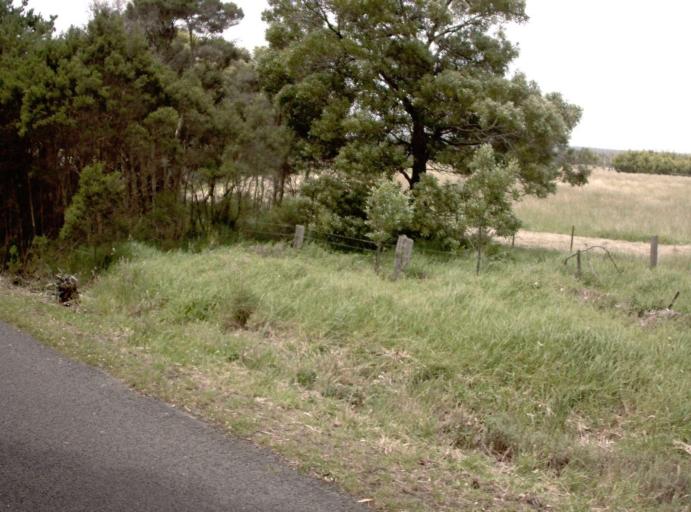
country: AU
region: Victoria
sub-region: Latrobe
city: Traralgon
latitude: -38.4841
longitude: 146.6811
